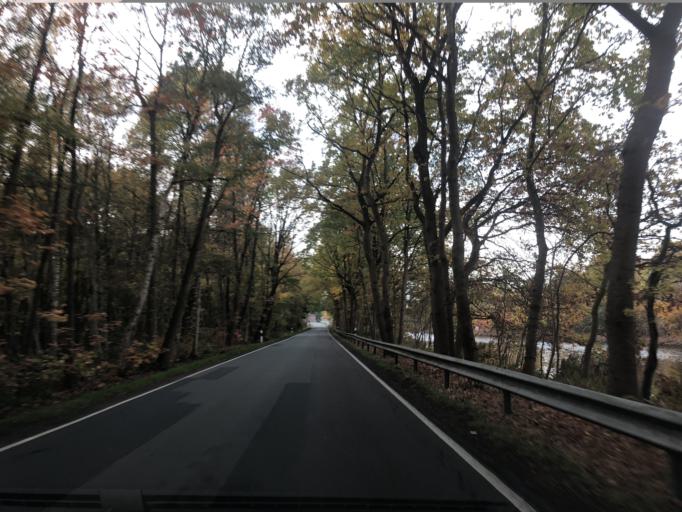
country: DE
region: Lower Saxony
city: Edewecht
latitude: 53.0863
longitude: 7.9443
